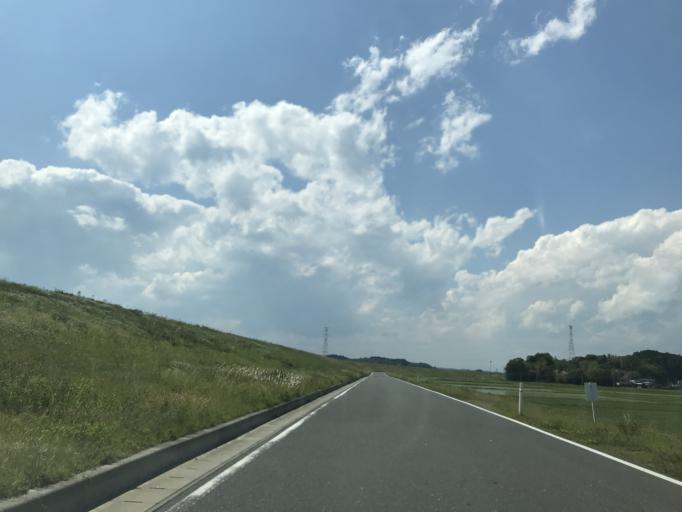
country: JP
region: Miyagi
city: Yamoto
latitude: 38.4224
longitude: 141.1309
